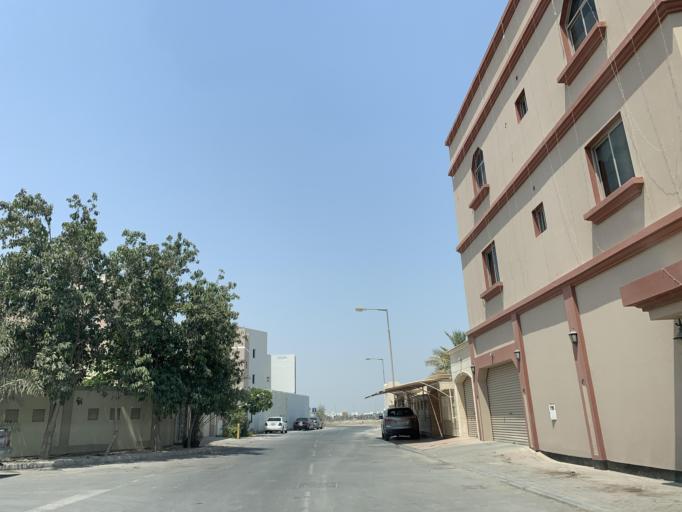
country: BH
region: Manama
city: Jidd Hafs
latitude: 26.2052
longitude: 50.5187
